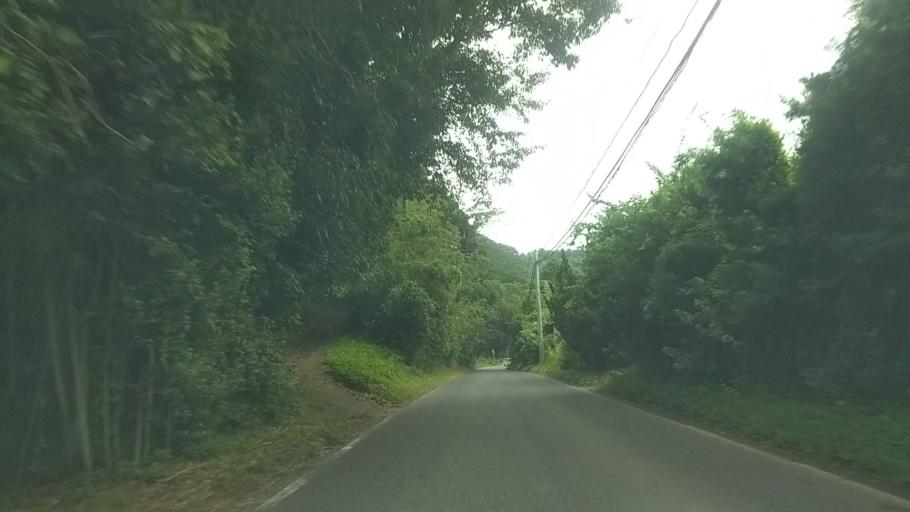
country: JP
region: Chiba
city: Kimitsu
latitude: 35.2292
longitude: 140.0133
